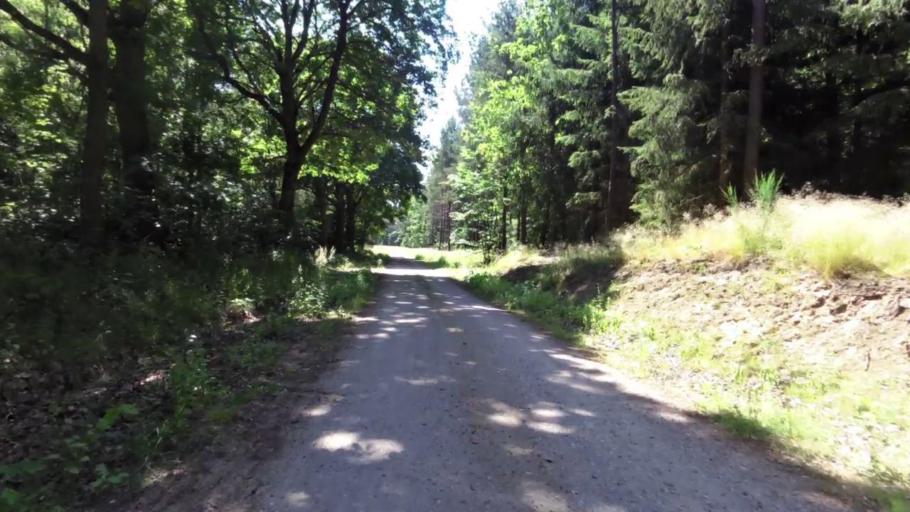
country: PL
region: West Pomeranian Voivodeship
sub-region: Powiat swidwinski
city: Polczyn-Zdroj
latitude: 53.7954
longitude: 16.1143
